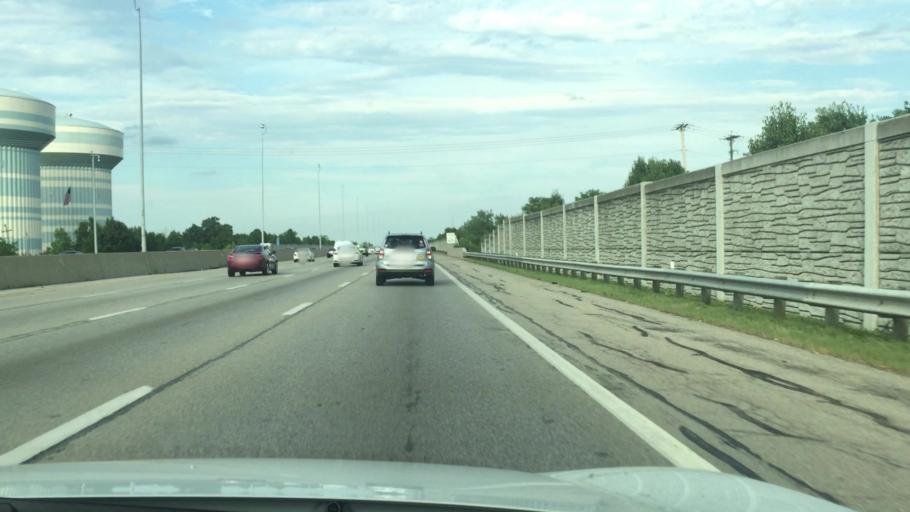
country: US
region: Ohio
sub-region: Delaware County
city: Powell
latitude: 40.1103
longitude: -83.0668
